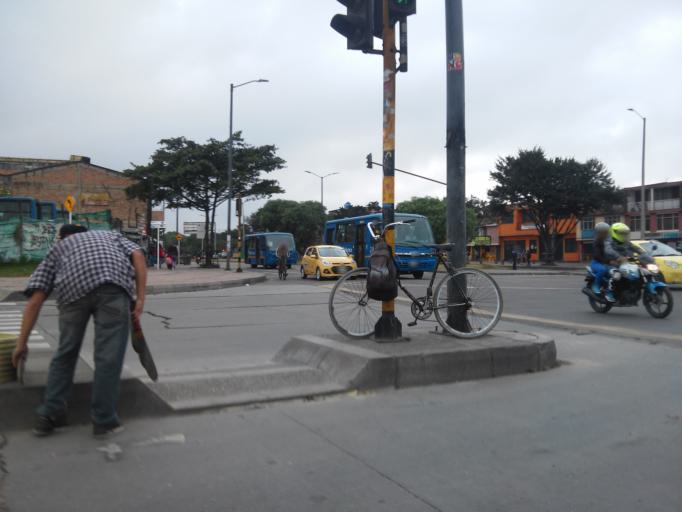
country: CO
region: Cundinamarca
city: Soacha
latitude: 4.6151
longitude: -74.1624
